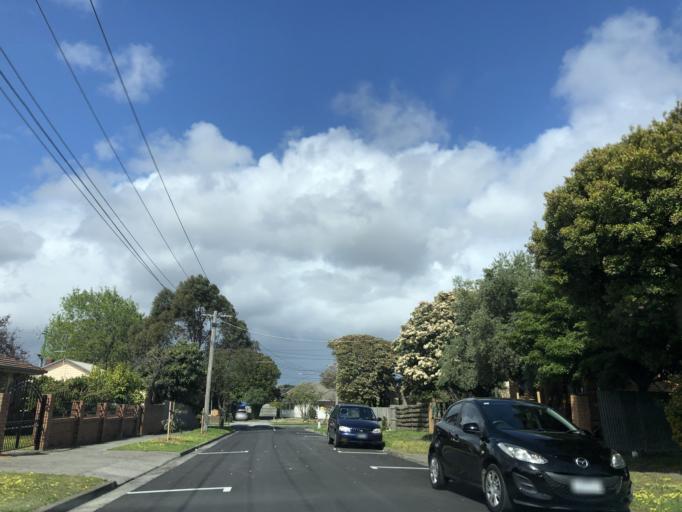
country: AU
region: Victoria
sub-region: Kingston
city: Clayton South
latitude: -37.9289
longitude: 145.1139
